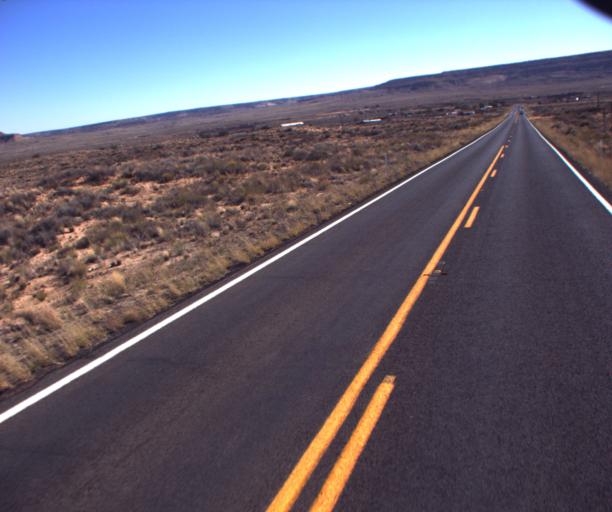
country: US
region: Arizona
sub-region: Navajo County
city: First Mesa
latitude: 35.8822
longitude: -110.6173
